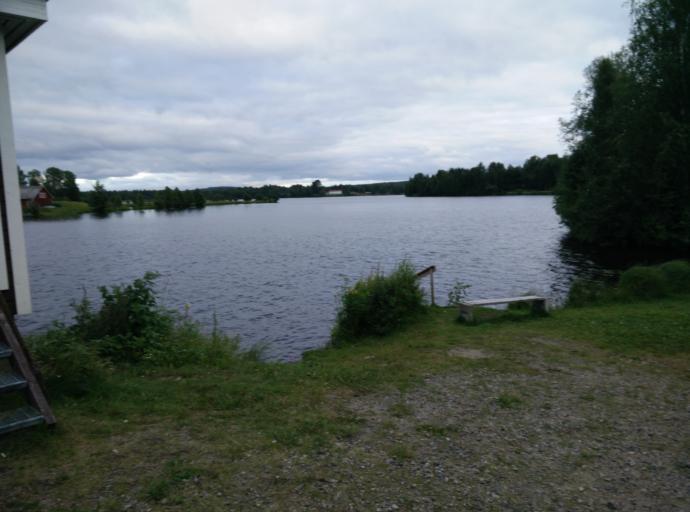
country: FI
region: Lapland
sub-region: Rovaniemi
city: Rovaniemi
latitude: 66.4883
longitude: 25.7288
